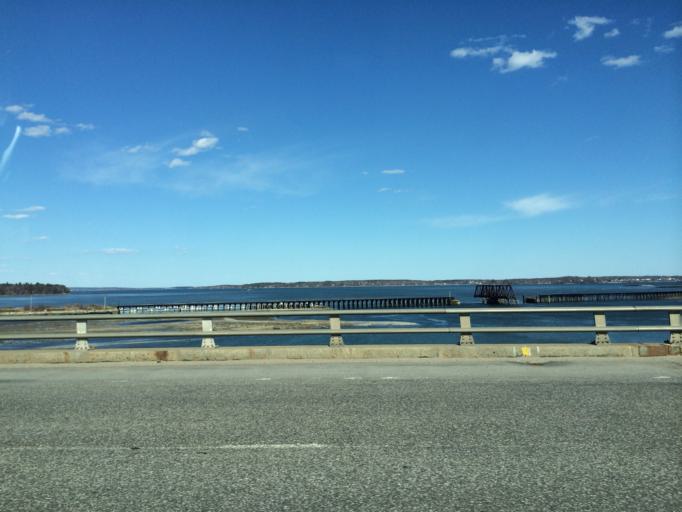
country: US
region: Maine
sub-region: Cumberland County
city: Portland
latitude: 43.6756
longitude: -70.2563
